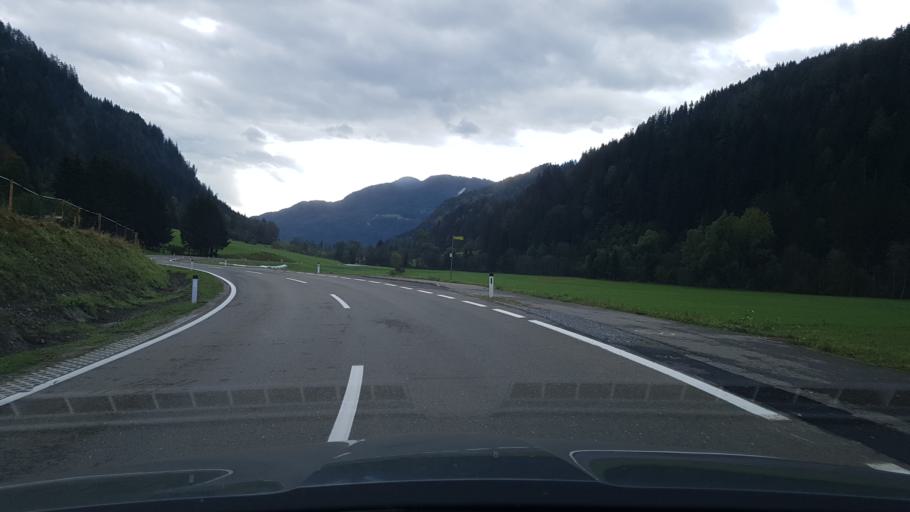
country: AT
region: Styria
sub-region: Politischer Bezirk Murau
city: Oberwolz Stadt
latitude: 47.1605
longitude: 14.2520
